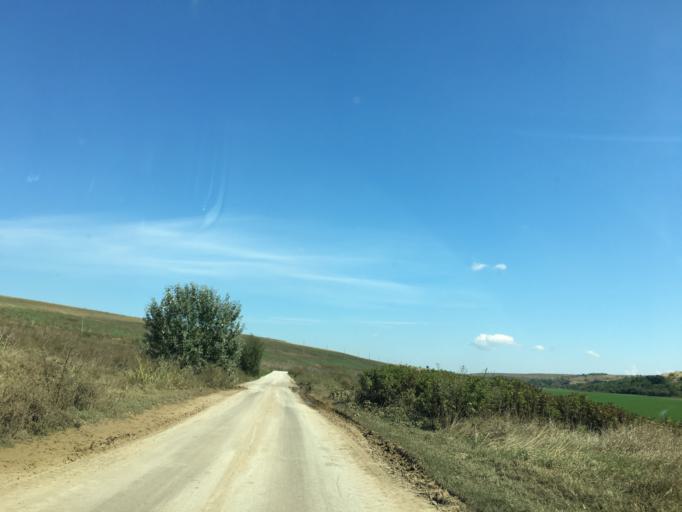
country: BG
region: Pleven
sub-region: Obshtina Knezha
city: Knezha
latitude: 43.5521
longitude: 24.1798
